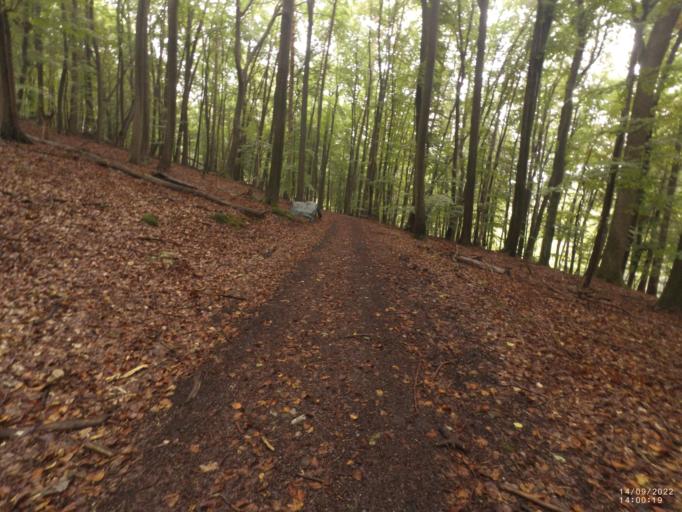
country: DE
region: Bavaria
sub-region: Regierungsbezirk Unterfranken
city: Glattbach
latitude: 50.0166
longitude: 9.1445
